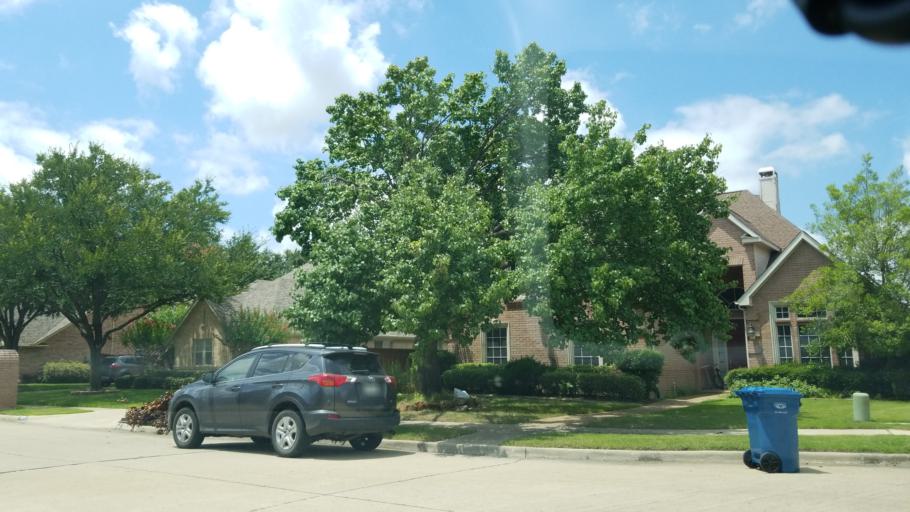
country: US
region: Texas
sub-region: Dallas County
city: Coppell
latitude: 32.9600
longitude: -96.9530
